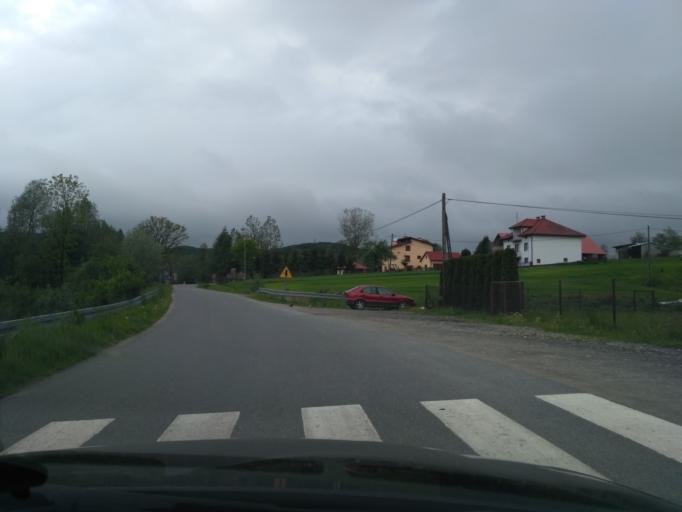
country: PL
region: Subcarpathian Voivodeship
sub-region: Powiat jasielski
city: Brzyska
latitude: 49.8535
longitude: 21.3408
